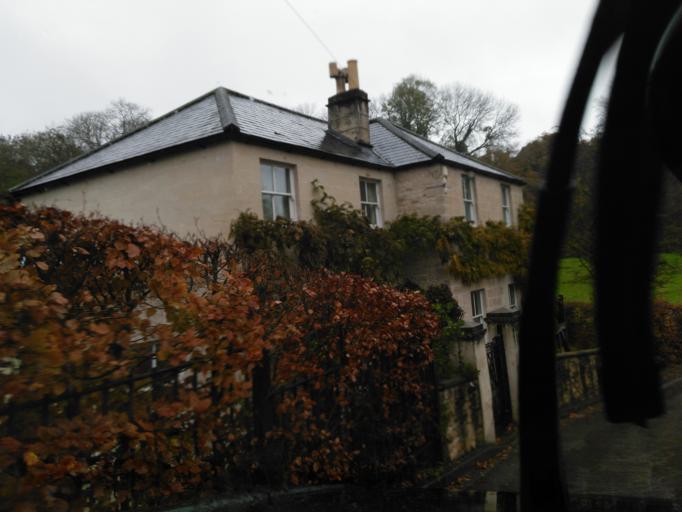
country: GB
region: England
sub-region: Bath and North East Somerset
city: Wellow
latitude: 51.3237
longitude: -2.3695
